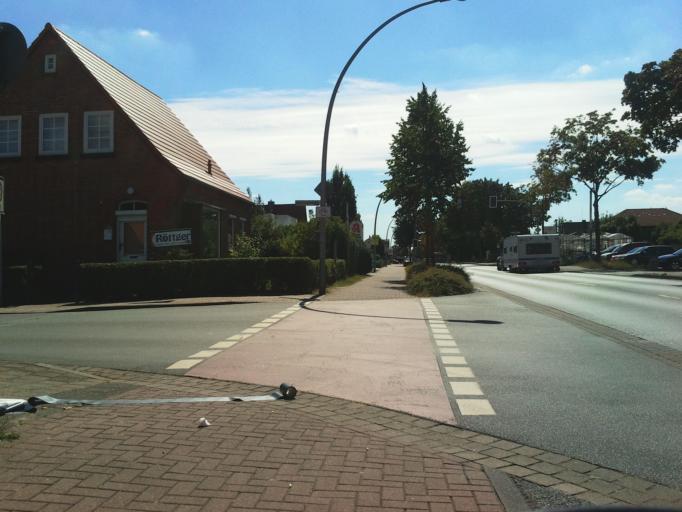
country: DE
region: Lower Saxony
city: Nienburg
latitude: 52.6624
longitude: 9.2218
